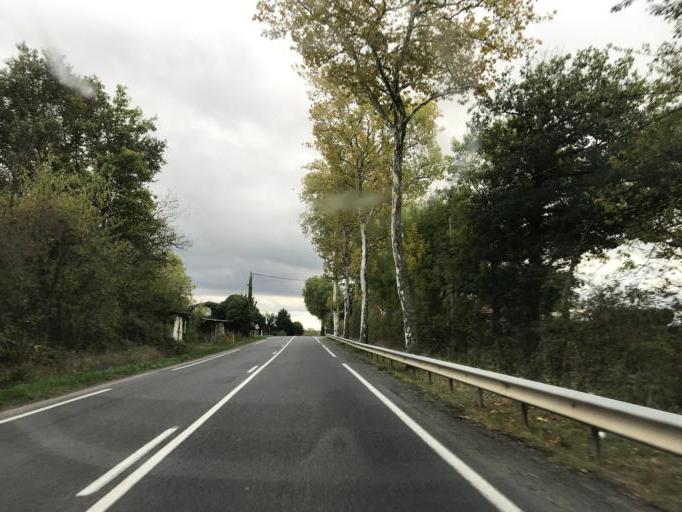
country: FR
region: Rhone-Alpes
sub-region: Departement de l'Ain
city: Chatillon-sur-Chalaronne
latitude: 46.0999
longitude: 4.9315
